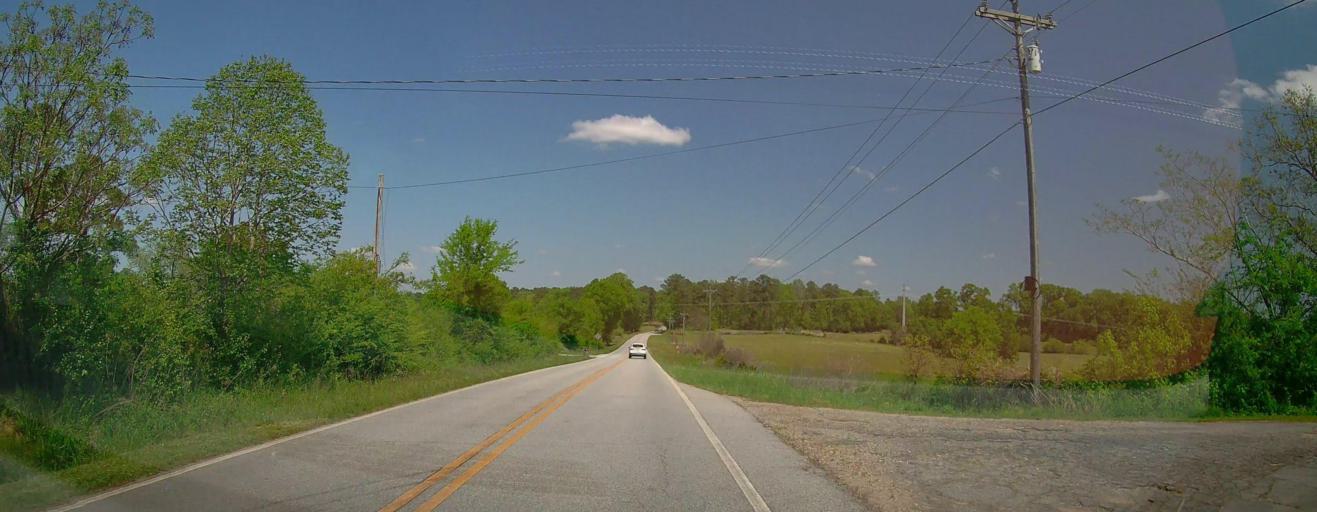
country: US
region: Georgia
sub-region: Bibb County
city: Macon
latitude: 32.9111
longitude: -83.6074
